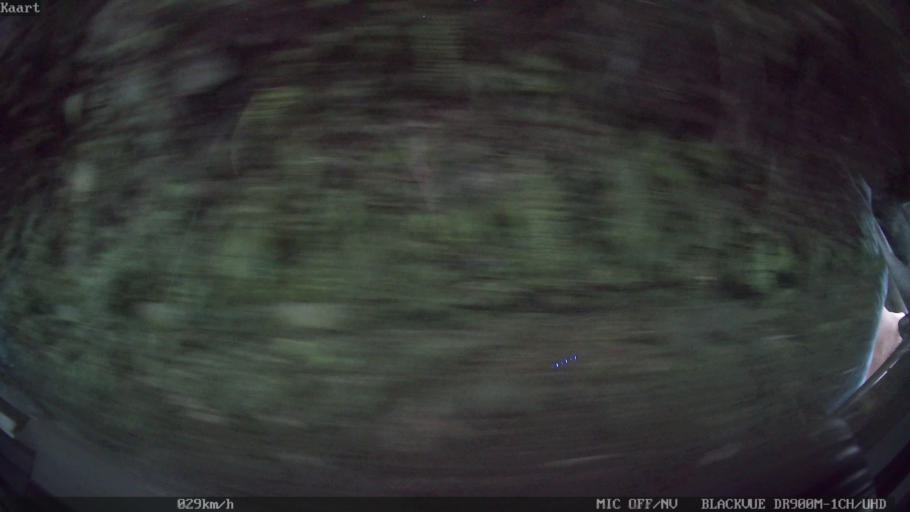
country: ID
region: Bali
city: Peneng
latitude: -8.3421
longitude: 115.1854
